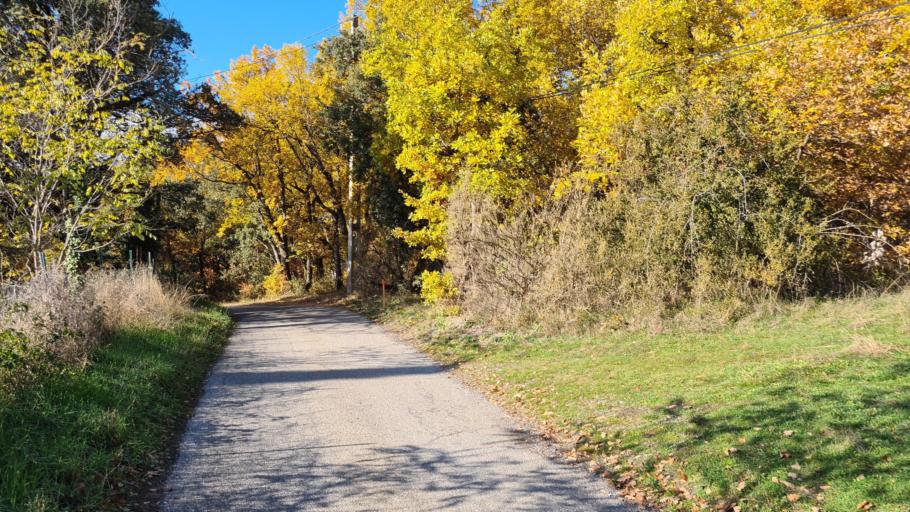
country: FR
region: Provence-Alpes-Cote d'Azur
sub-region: Departement des Alpes-de-Haute-Provence
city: Le Brusquet
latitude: 44.1621
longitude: 6.3041
